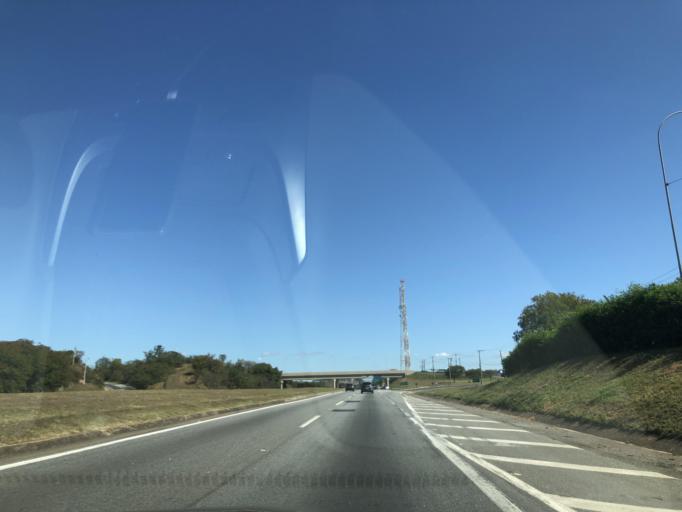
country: BR
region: Sao Paulo
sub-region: Sorocaba
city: Sorocaba
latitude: -23.4375
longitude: -47.3769
